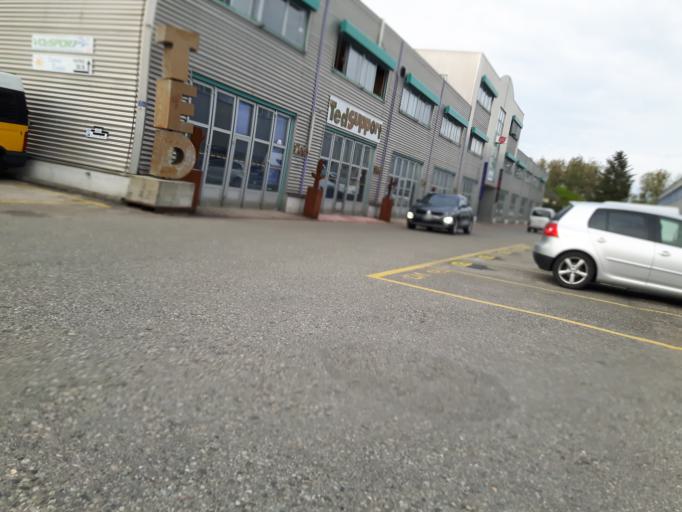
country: CH
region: Vaud
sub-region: Jura-Nord vaudois District
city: Yverdon-les-Bains
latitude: 46.7912
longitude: 6.6322
